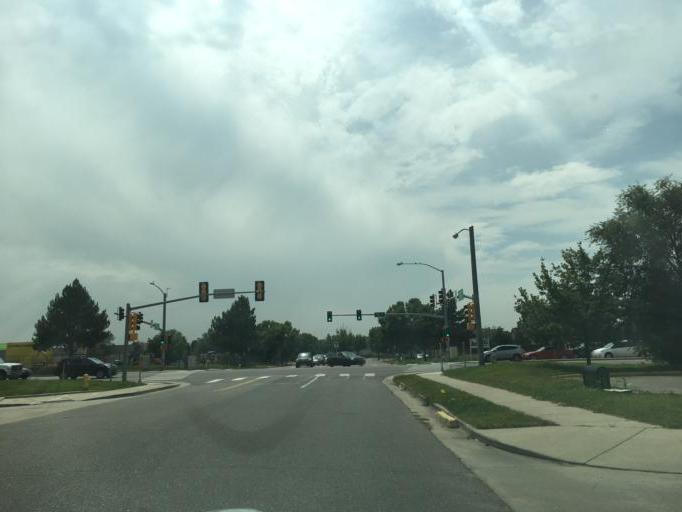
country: US
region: Colorado
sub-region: Adams County
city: Aurora
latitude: 39.7261
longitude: -104.8082
